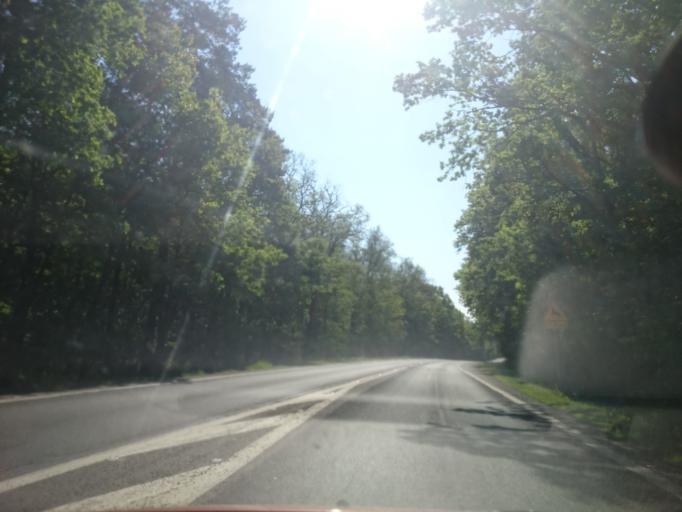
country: PL
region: Opole Voivodeship
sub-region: Powiat opolski
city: Chrzastowice
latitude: 50.6213
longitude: 18.0555
